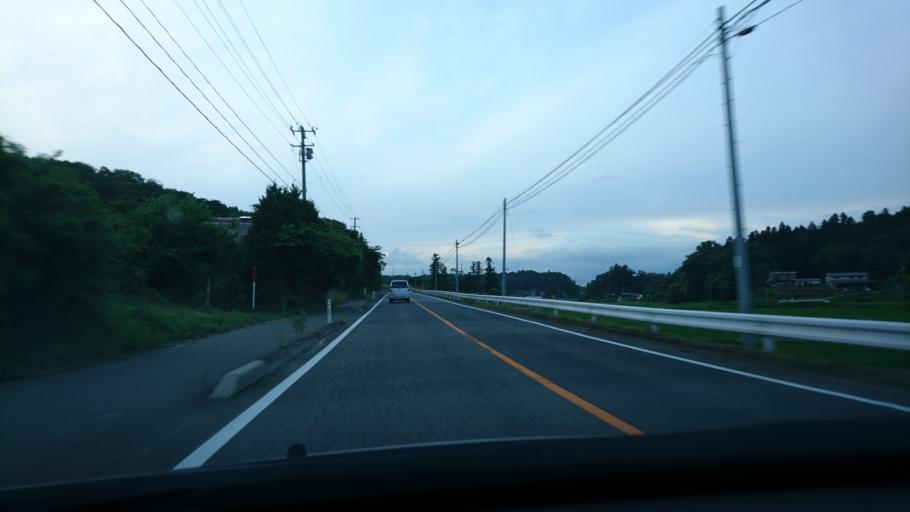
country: JP
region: Miyagi
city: Furukawa
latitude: 38.7645
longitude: 141.0037
